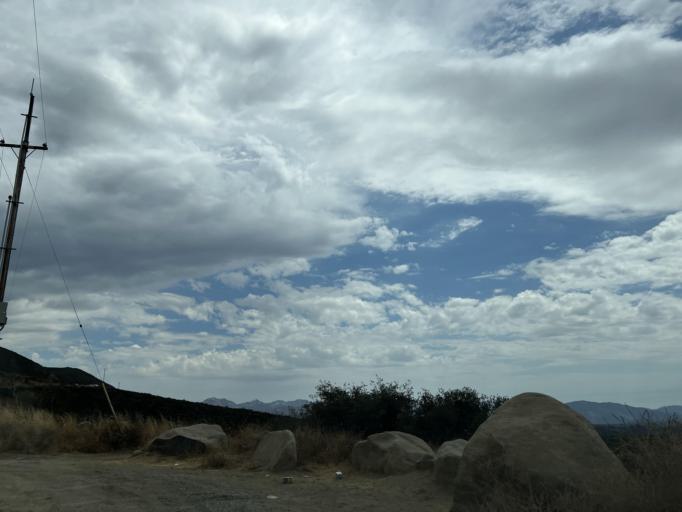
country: US
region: California
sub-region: San Diego County
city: Alpine
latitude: 32.8596
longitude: -116.7437
